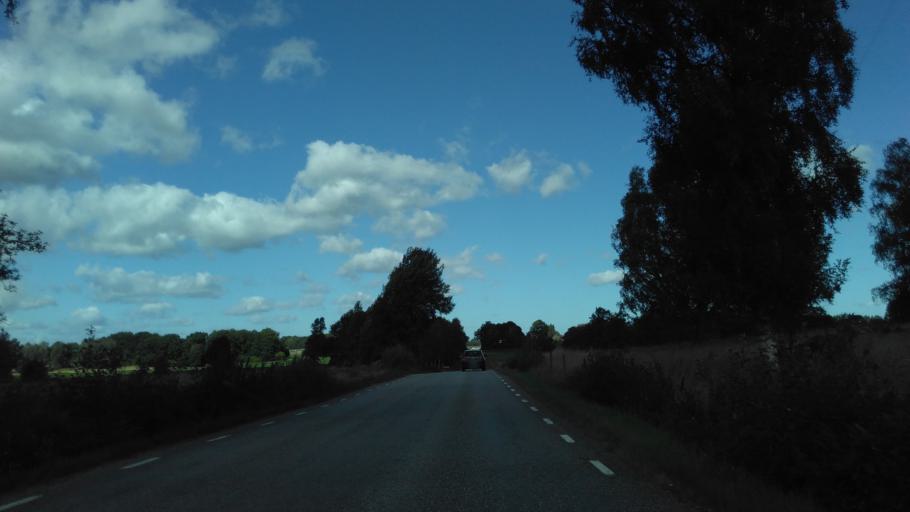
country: SE
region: Vaestra Goetaland
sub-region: Herrljunga Kommun
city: Herrljunga
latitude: 58.1486
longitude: 13.0187
